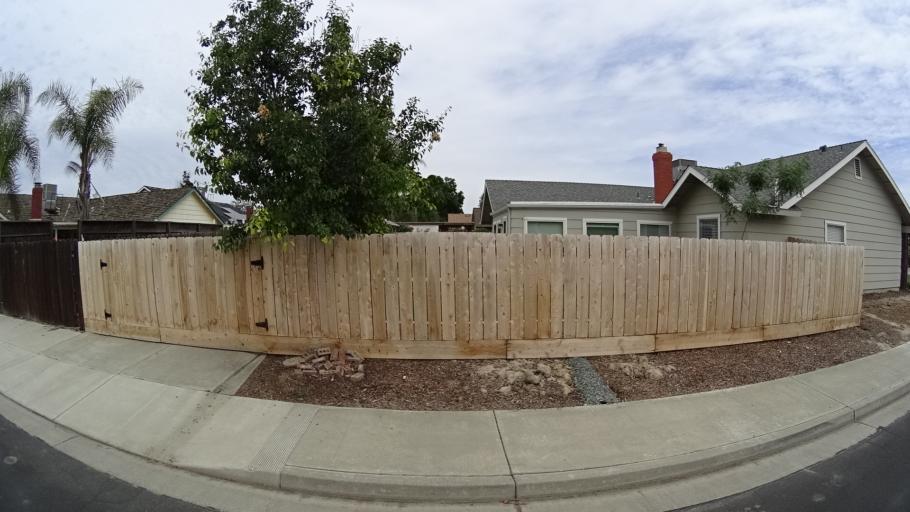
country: US
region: California
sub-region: Kings County
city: Hanford
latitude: 36.3595
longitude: -119.6392
